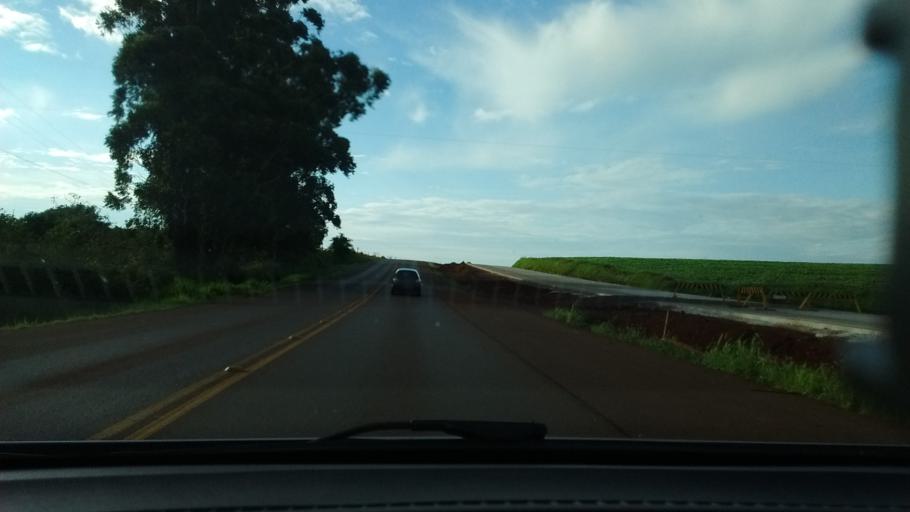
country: BR
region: Parana
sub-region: Cascavel
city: Cascavel
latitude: -25.1004
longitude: -53.5932
